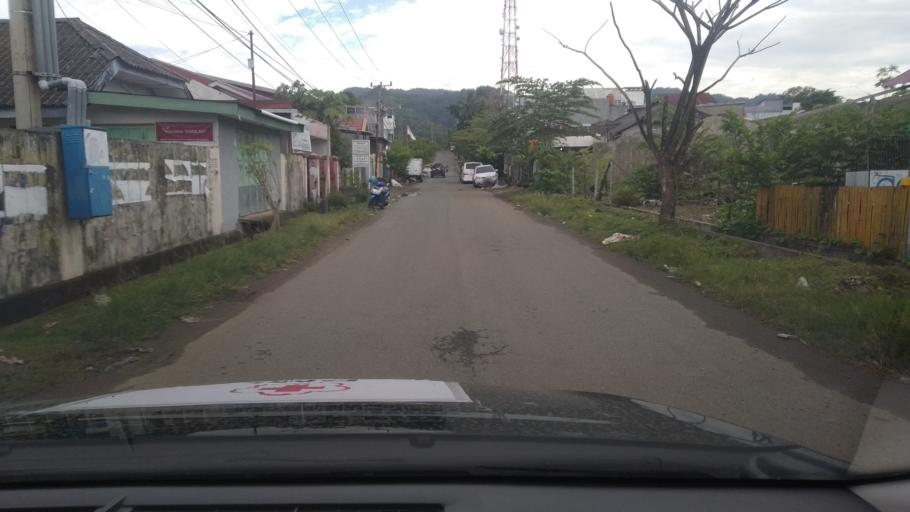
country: ID
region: Sulawesi Barat
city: Mamuju
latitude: -2.6801
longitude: 118.8830
